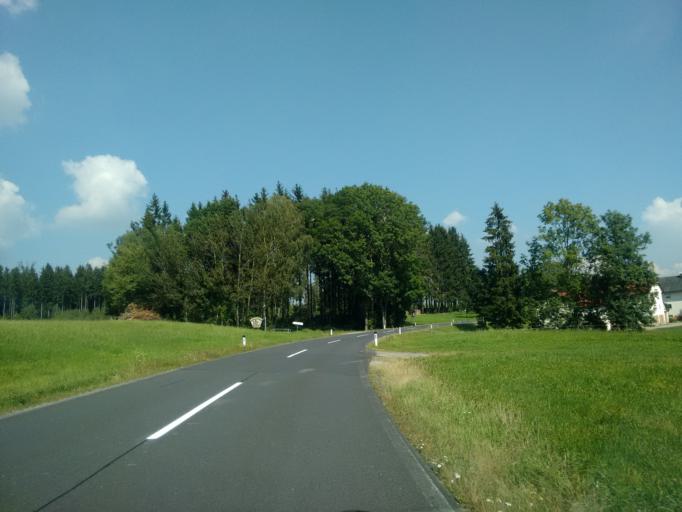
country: AT
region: Upper Austria
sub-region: Politischer Bezirk Urfahr-Umgebung
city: Altenberg bei Linz
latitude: 48.4011
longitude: 14.3428
